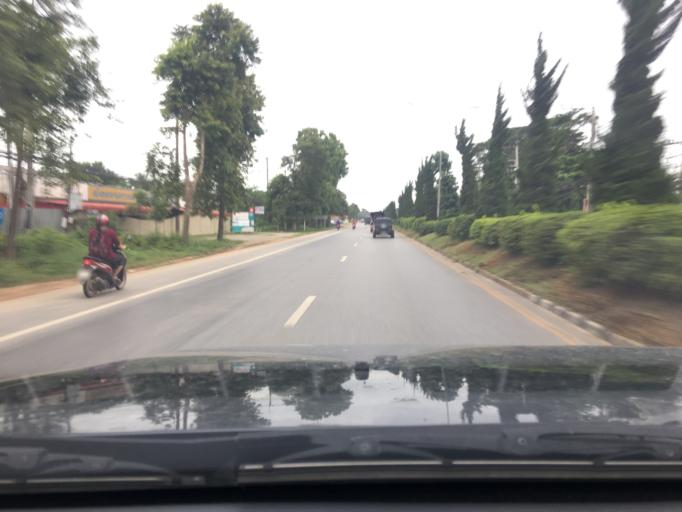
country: TH
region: Chiang Rai
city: Chiang Rai
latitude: 19.9496
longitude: 99.8486
